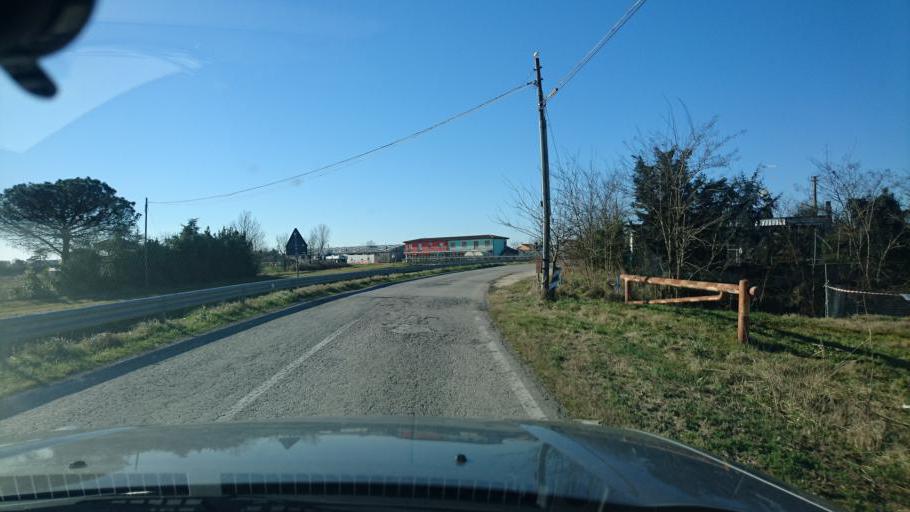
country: IT
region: Emilia-Romagna
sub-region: Provincia di Ferrara
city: Mesola
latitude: 44.9389
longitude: 12.2283
